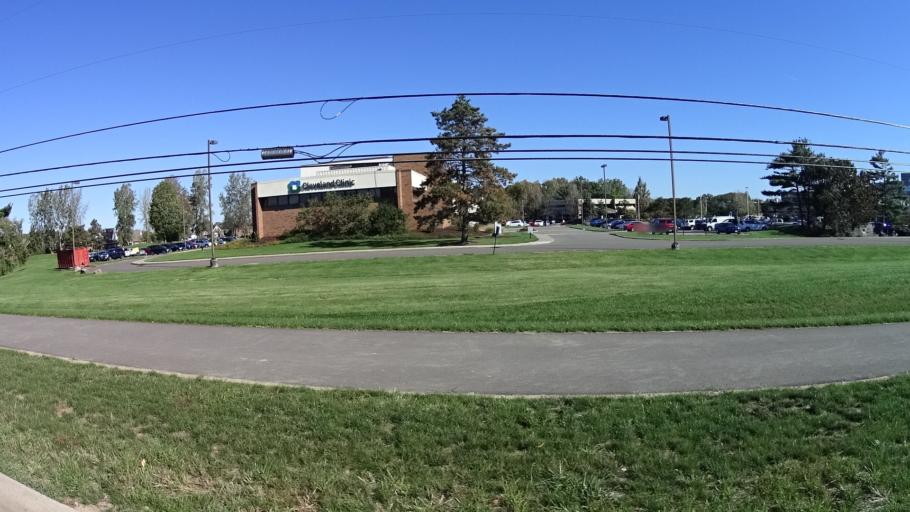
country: US
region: Ohio
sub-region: Lorain County
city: Amherst
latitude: 41.4120
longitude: -82.2376
